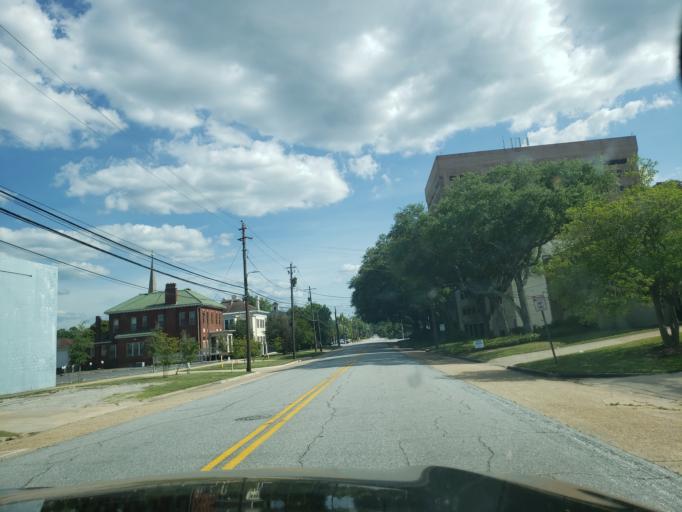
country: US
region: Georgia
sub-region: Muscogee County
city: Columbus
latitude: 32.4701
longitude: -84.9890
